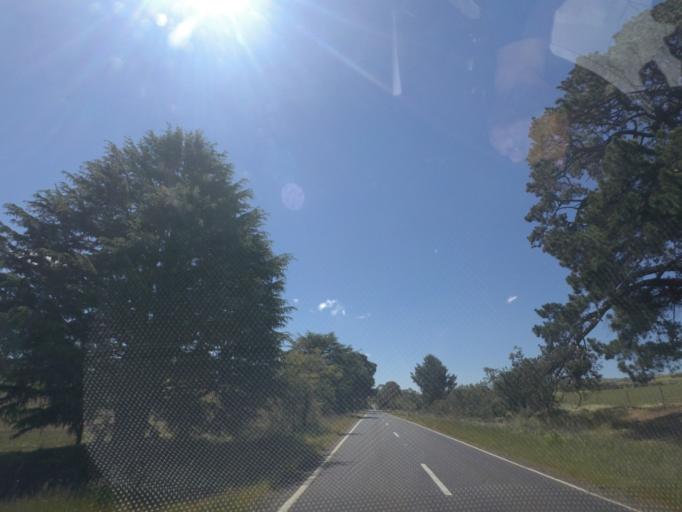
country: AU
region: Victoria
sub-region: Hume
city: Sunbury
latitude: -37.1095
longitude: 144.7594
